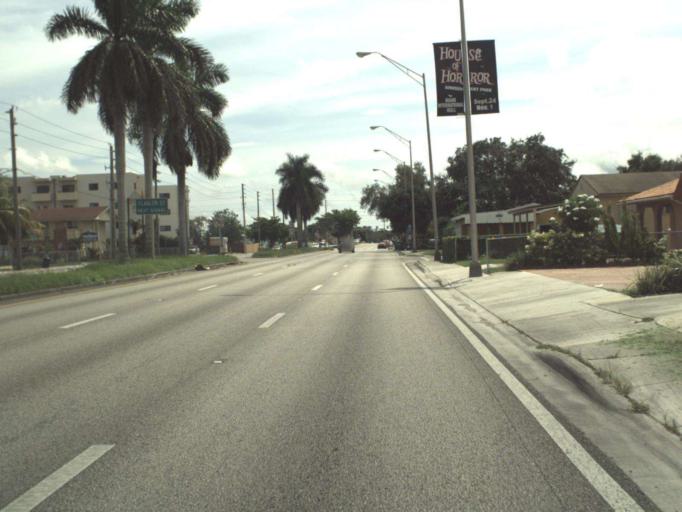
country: US
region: Florida
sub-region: Miami-Dade County
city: Flagami
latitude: 25.7736
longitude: -80.3124
